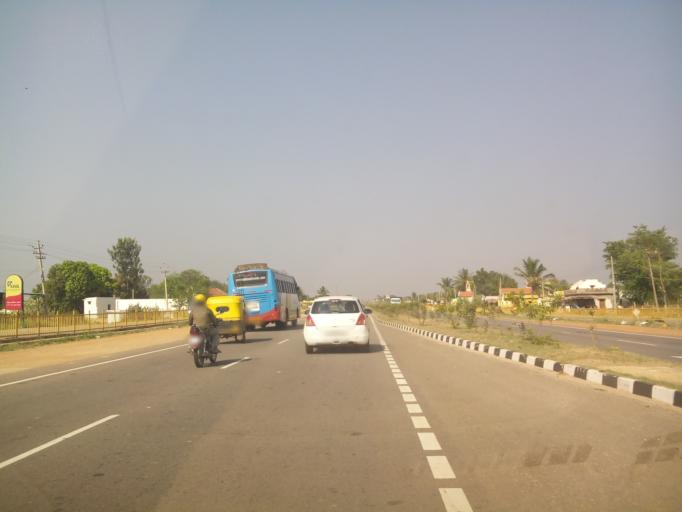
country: IN
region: Karnataka
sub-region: Tumkur
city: Kunigal
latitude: 12.9935
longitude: 76.8953
